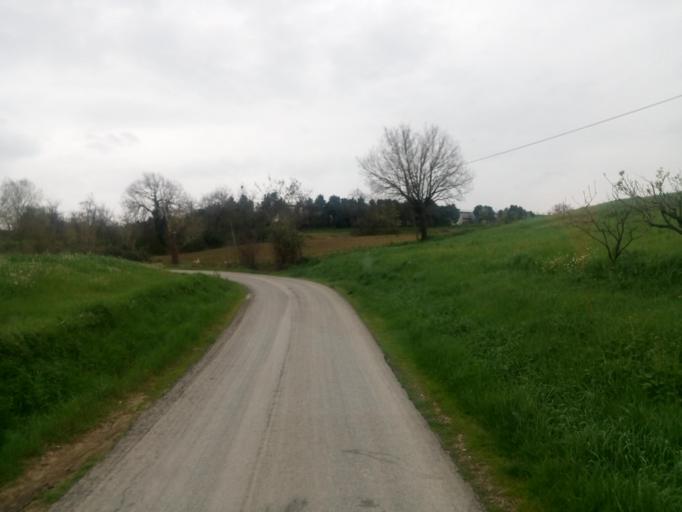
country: IT
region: Emilia-Romagna
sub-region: Forli-Cesena
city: Meldola
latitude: 44.1243
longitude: 12.0770
